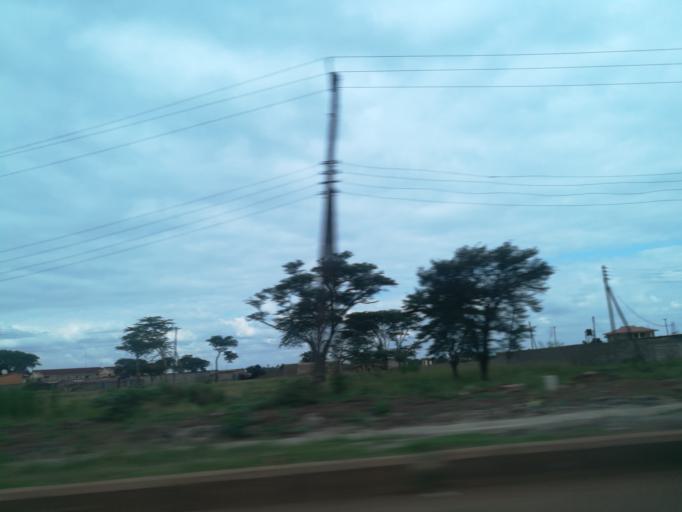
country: KE
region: Nairobi Area
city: Thika
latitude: -1.0934
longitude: 37.0314
